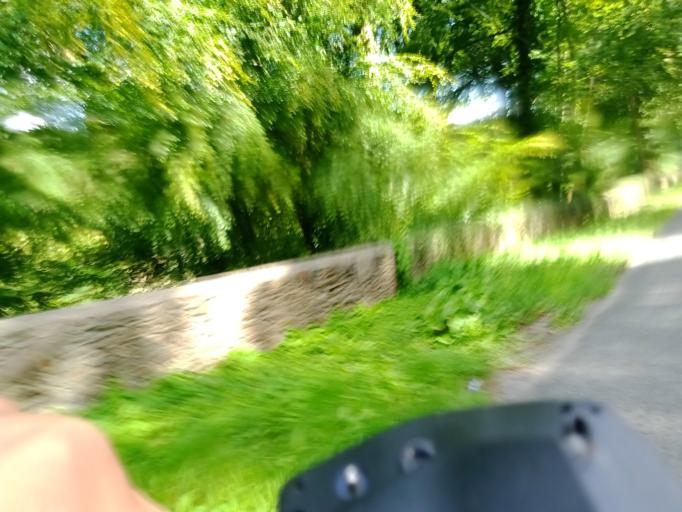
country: IE
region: Munster
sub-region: Waterford
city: Dungarvan
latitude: 52.1227
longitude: -7.4716
